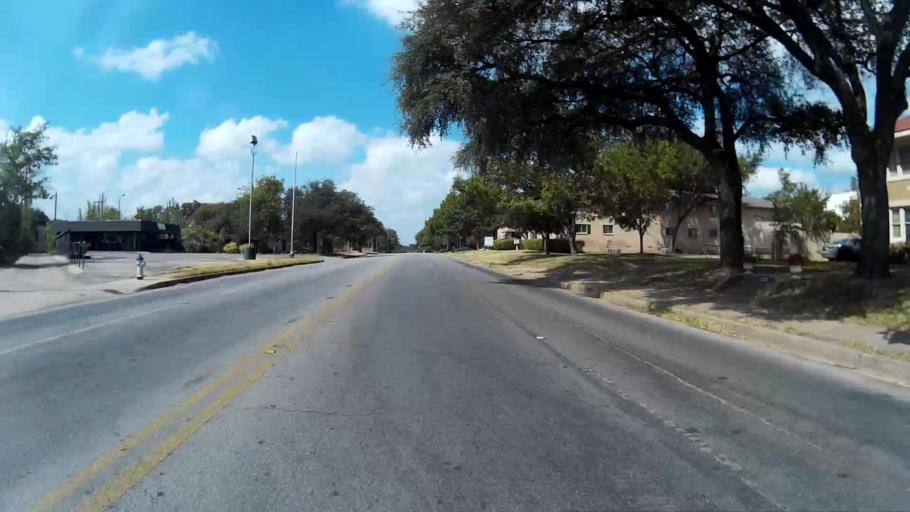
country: US
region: Texas
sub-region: Dallas County
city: Highland Park
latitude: 32.8127
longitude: -96.7553
